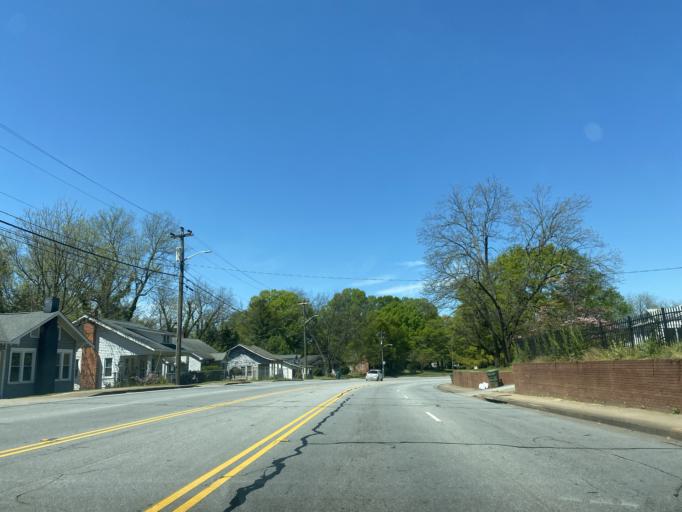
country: US
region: South Carolina
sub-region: Cherokee County
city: Gaffney
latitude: 35.0616
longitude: -81.6430
